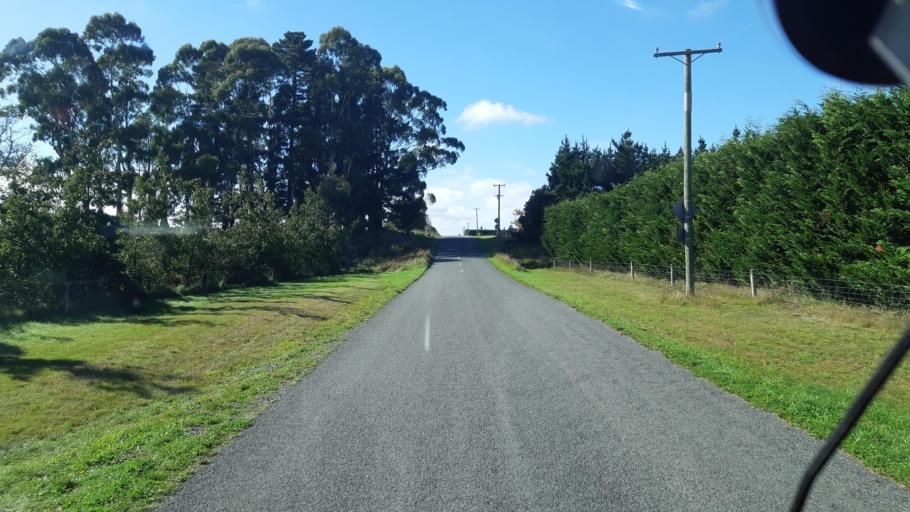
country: NZ
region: Canterbury
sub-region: Waimakariri District
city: Woodend
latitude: -43.2663
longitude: 172.4936
